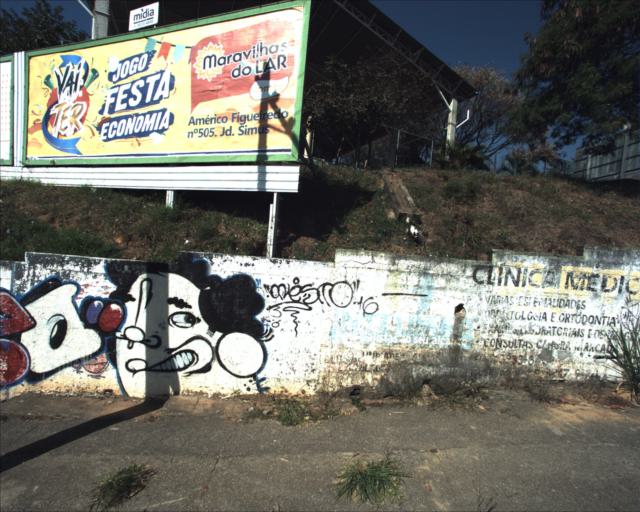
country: BR
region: Sao Paulo
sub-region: Sorocaba
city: Sorocaba
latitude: -23.5018
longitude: -47.4792
